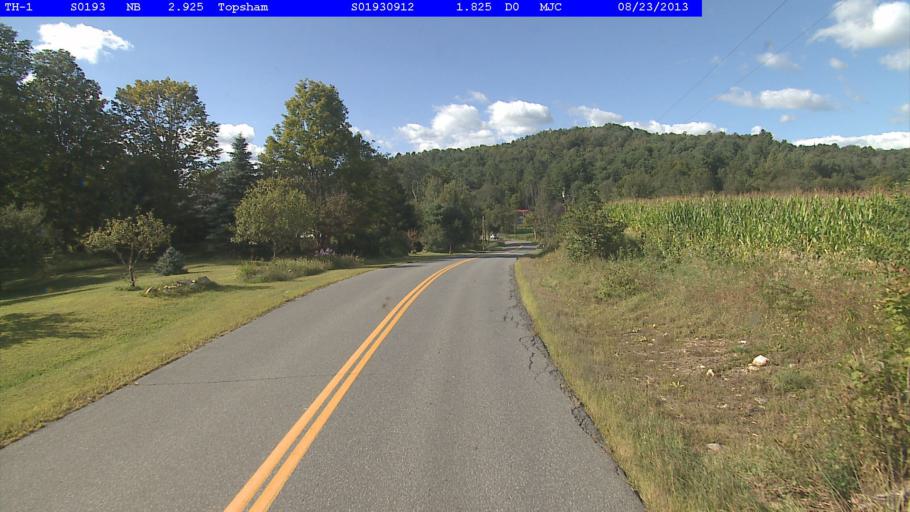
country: US
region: New Hampshire
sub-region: Grafton County
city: Haverhill
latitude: 44.0962
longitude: -72.2232
